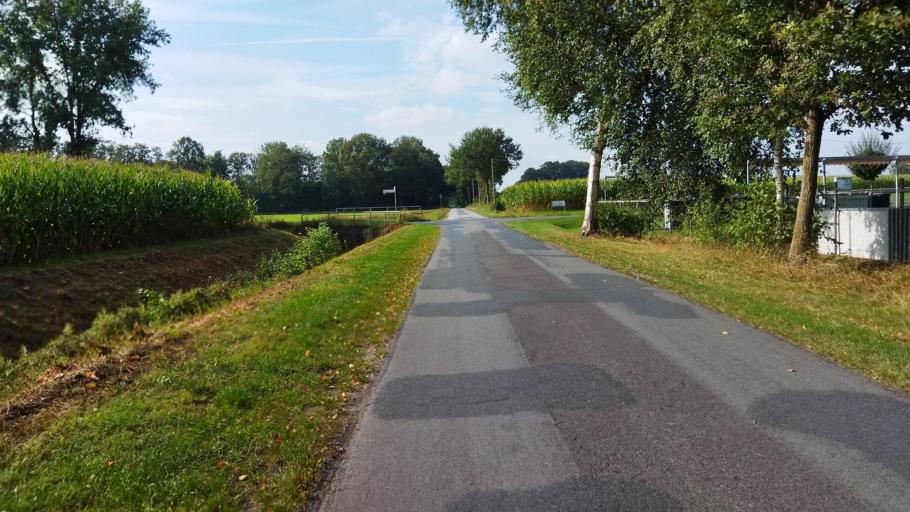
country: DE
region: North Rhine-Westphalia
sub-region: Regierungsbezirk Munster
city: Sassenberg
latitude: 52.0014
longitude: 8.0184
